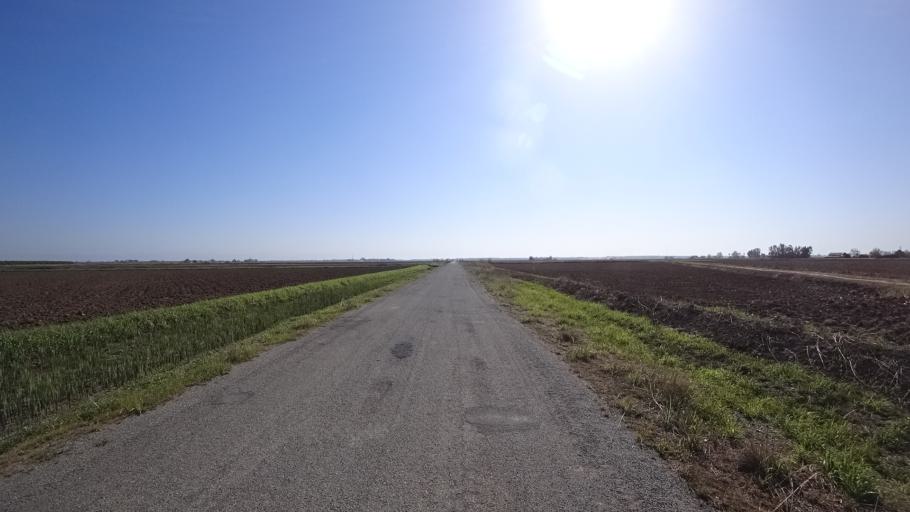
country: US
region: California
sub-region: Glenn County
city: Hamilton City
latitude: 39.6015
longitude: -122.0491
